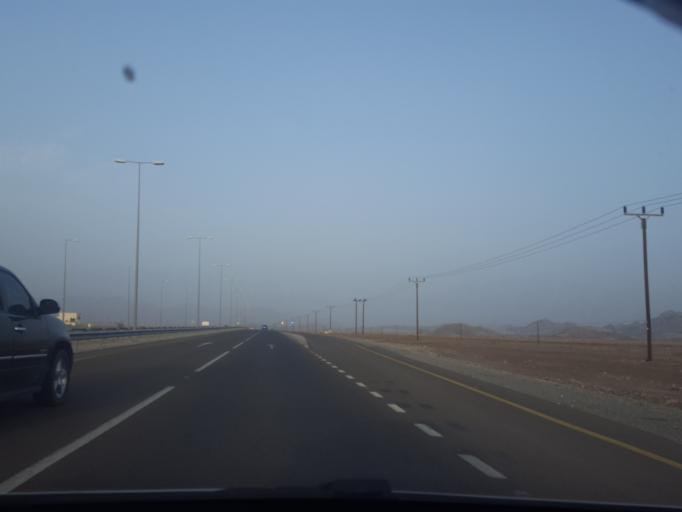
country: OM
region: Al Buraimi
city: Al Buraymi
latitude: 24.2466
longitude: 56.0209
